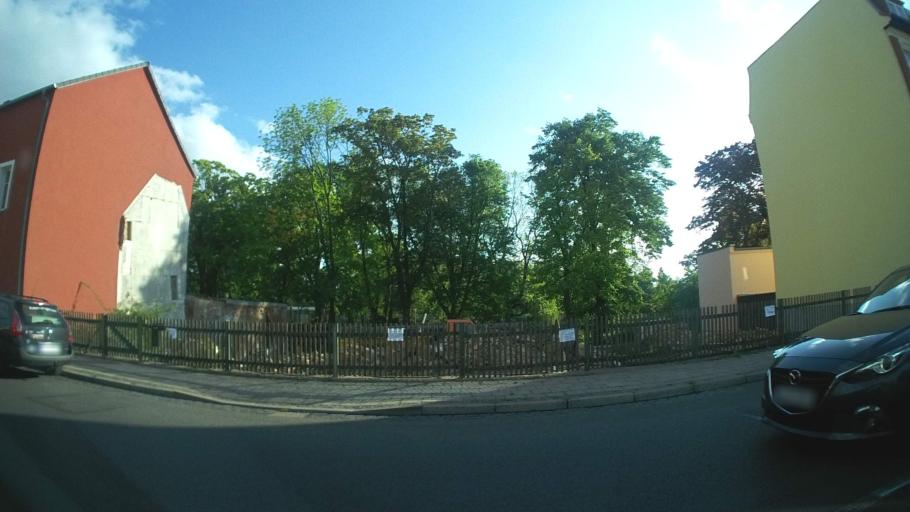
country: DE
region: Saxony
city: Grossposna
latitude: 51.2833
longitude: 12.4593
